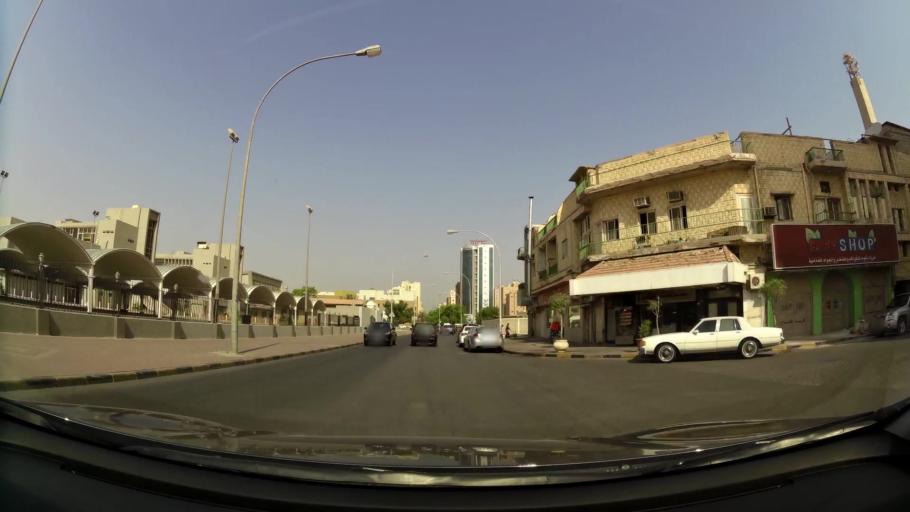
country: KW
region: Muhafazat Hawalli
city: Hawalli
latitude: 29.3330
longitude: 48.0146
